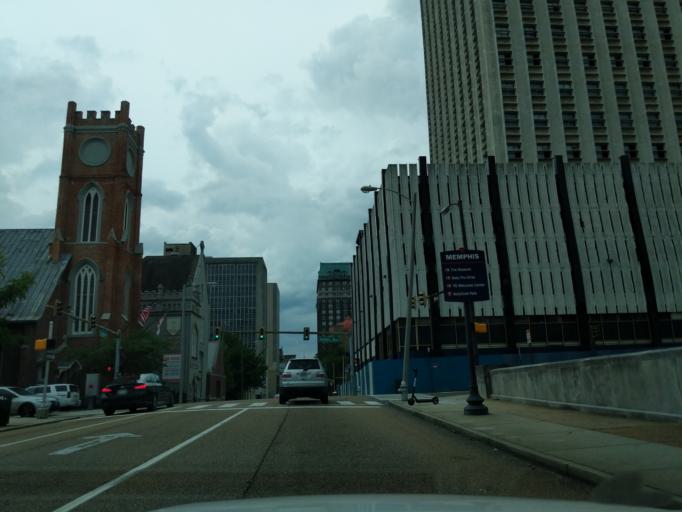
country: US
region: Tennessee
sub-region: Shelby County
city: Memphis
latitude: 35.1483
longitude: -90.0503
